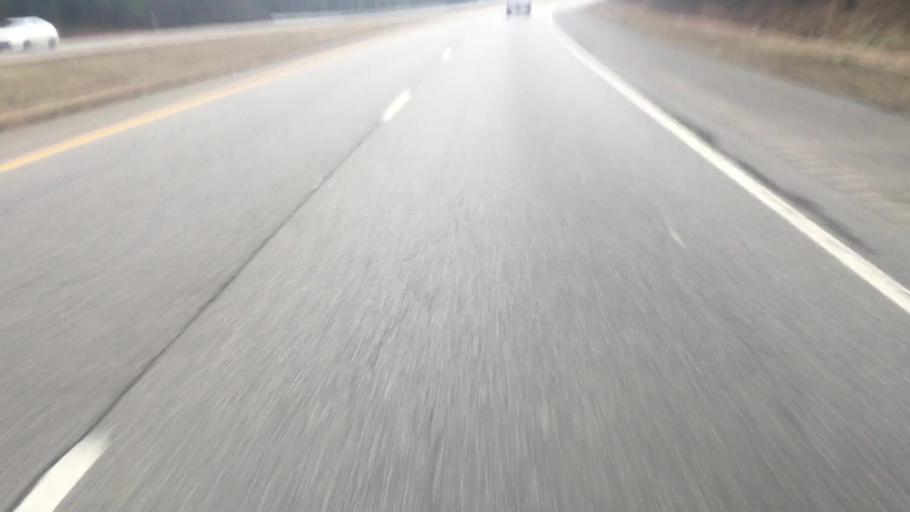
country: US
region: Alabama
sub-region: Walker County
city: Sumiton
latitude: 33.7218
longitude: -87.0023
